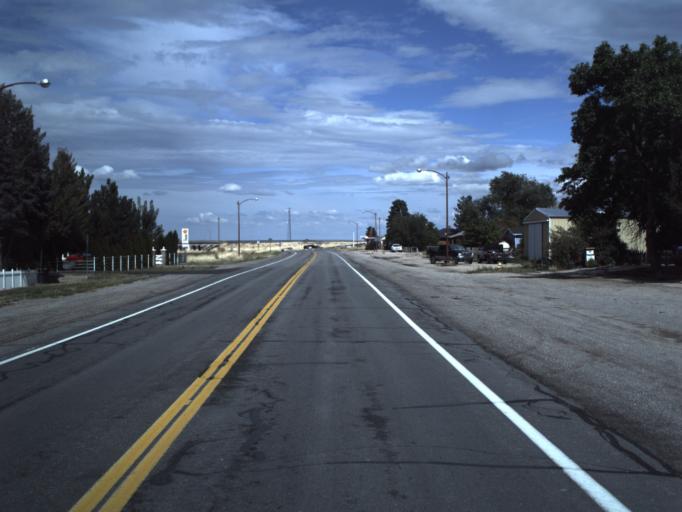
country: US
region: Utah
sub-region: Millard County
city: Fillmore
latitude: 38.8889
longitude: -112.4106
